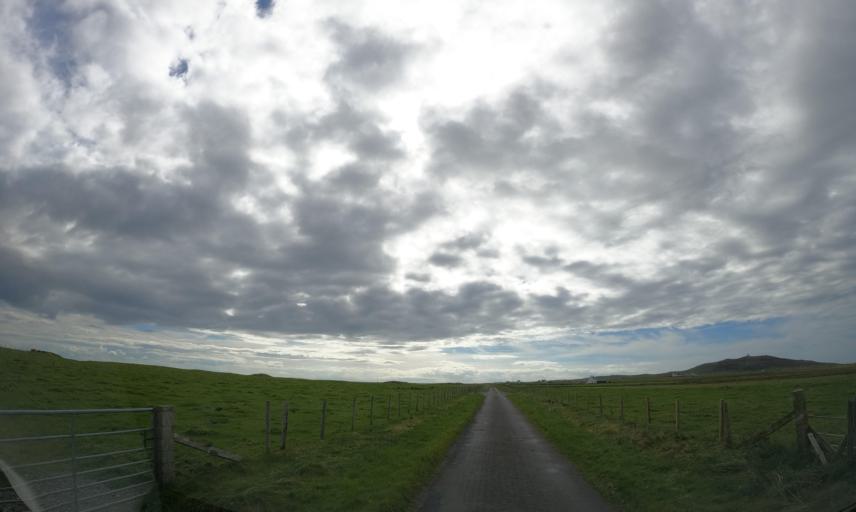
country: GB
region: Scotland
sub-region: Eilean Siar
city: Barra
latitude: 56.4816
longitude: -6.9009
